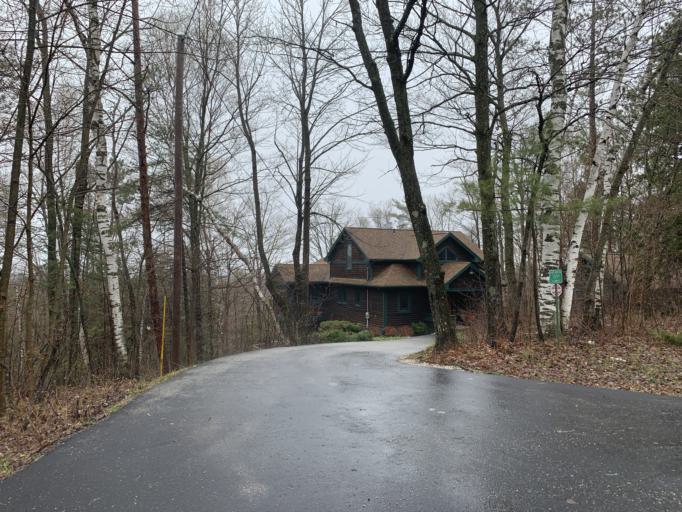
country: US
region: Wisconsin
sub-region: Door County
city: Sturgeon Bay
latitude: 44.9577
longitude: -87.3652
